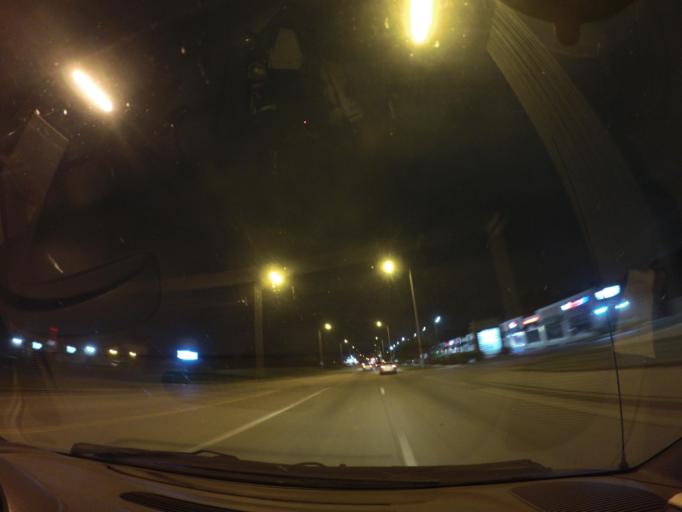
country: US
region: Illinois
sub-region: Cook County
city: Harvey
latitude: 41.6008
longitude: -87.6629
